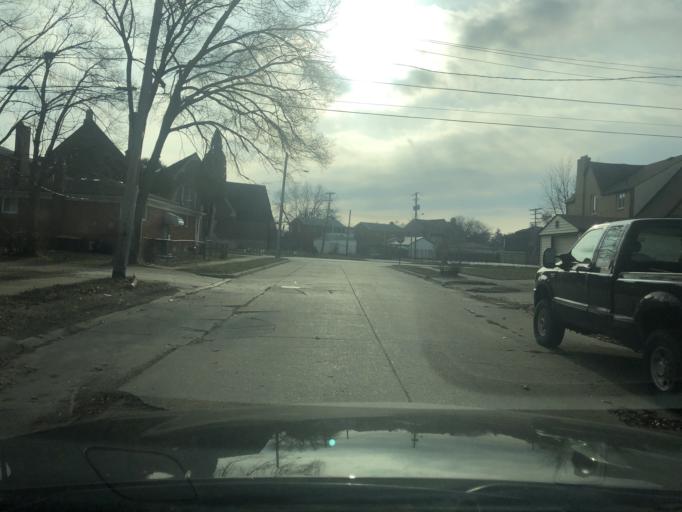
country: US
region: Michigan
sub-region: Wayne County
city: Highland Park
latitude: 42.3973
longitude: -83.1284
